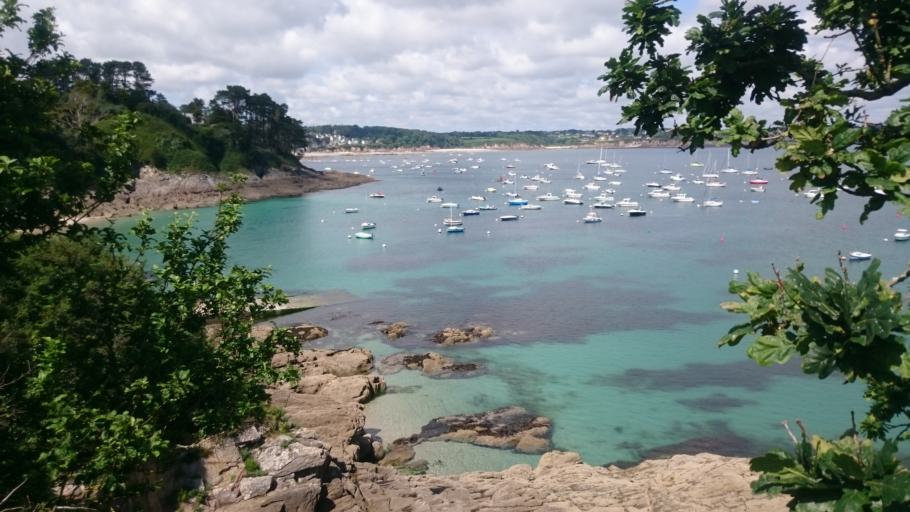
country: FR
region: Brittany
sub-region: Departement du Finistere
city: Plougonvelin
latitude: 48.3388
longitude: -4.6990
